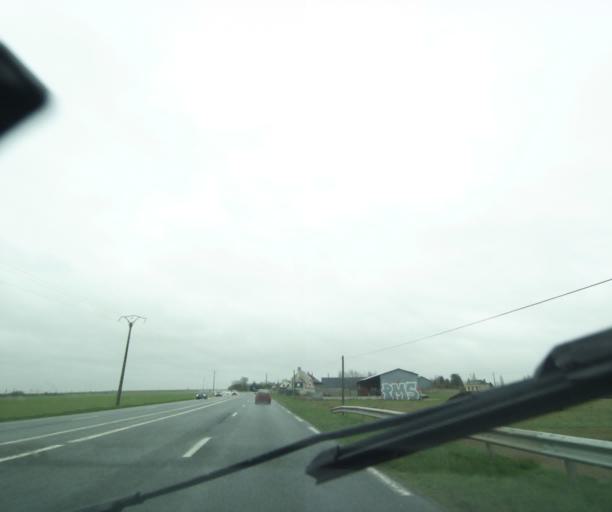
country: FR
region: Centre
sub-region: Departement du Loiret
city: Chevilly
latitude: 48.0542
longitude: 1.8756
